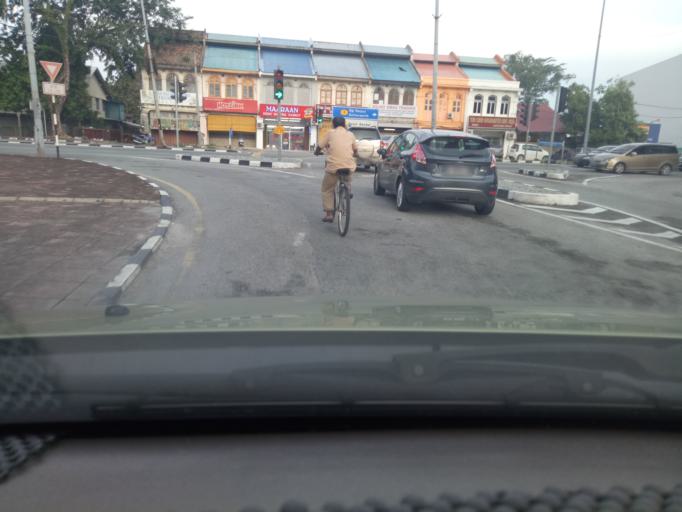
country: MY
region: Kedah
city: Alor Setar
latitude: 6.1132
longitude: 100.3643
